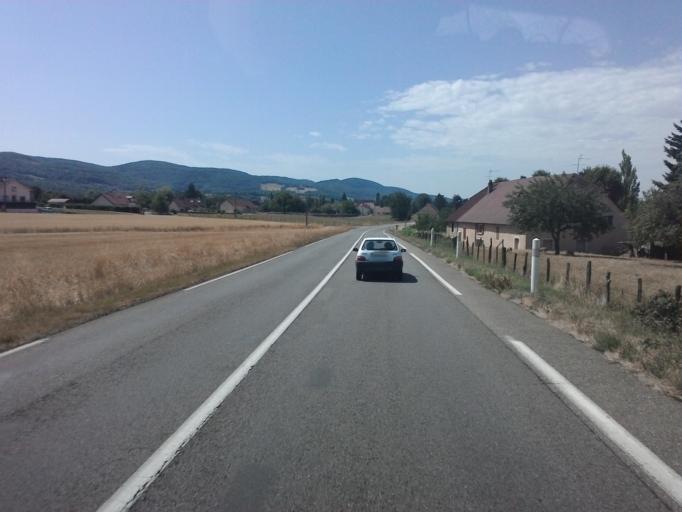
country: FR
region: Franche-Comte
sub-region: Departement du Jura
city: Montmorot
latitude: 46.6137
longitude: 5.4772
